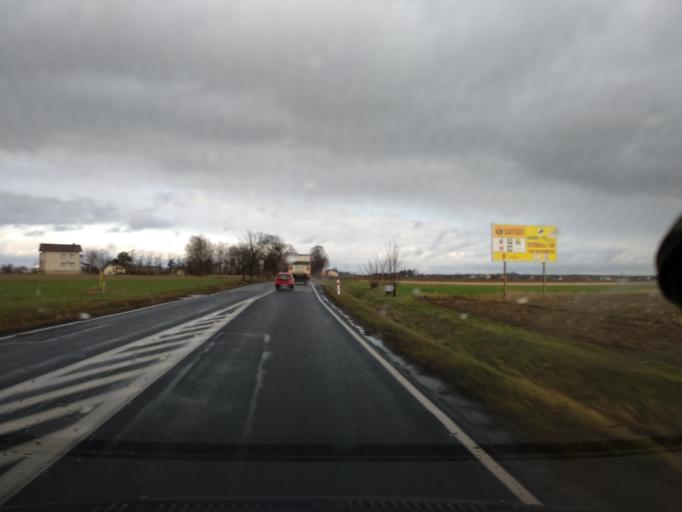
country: PL
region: Greater Poland Voivodeship
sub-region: Powiat koninski
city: Stare Miasto
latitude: 52.1478
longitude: 18.1996
